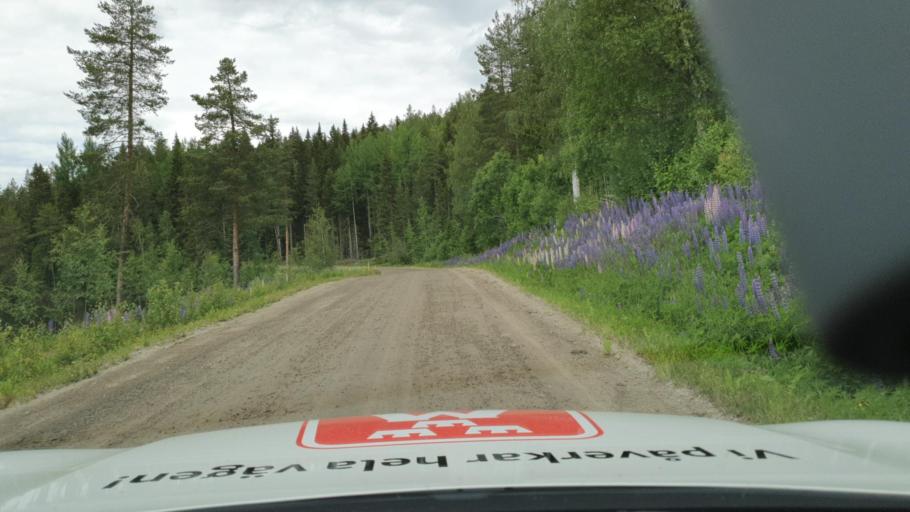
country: SE
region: Vaesterbotten
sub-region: Bjurholms Kommun
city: Bjurholm
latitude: 63.8363
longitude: 18.9996
